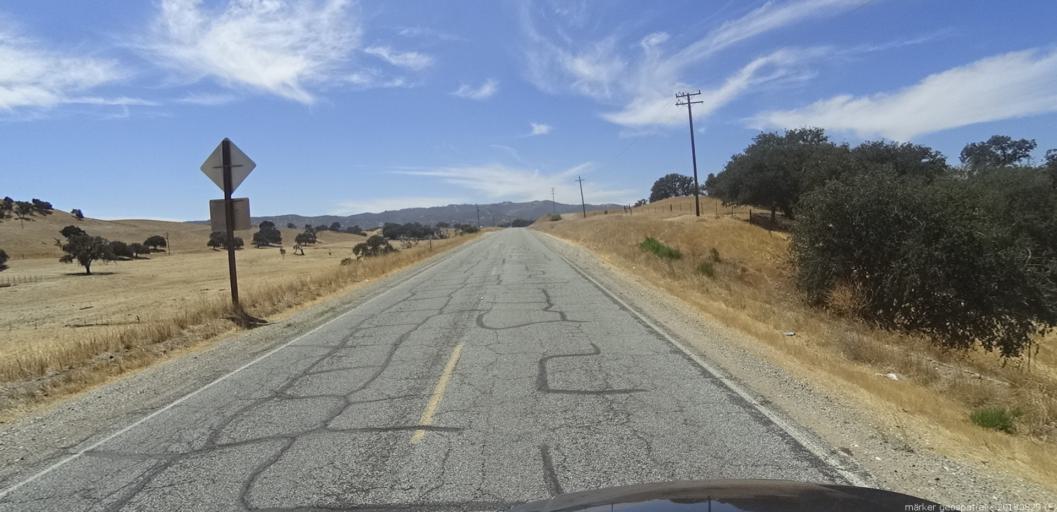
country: US
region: California
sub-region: San Luis Obispo County
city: Lake Nacimiento
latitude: 35.8714
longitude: -120.8410
